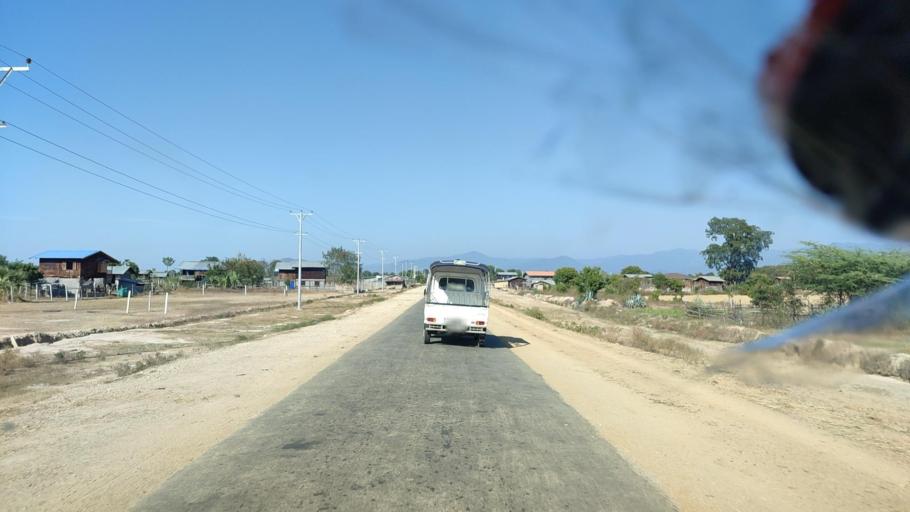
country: MM
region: Mandalay
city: Yamethin
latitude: 20.1678
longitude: 96.2601
